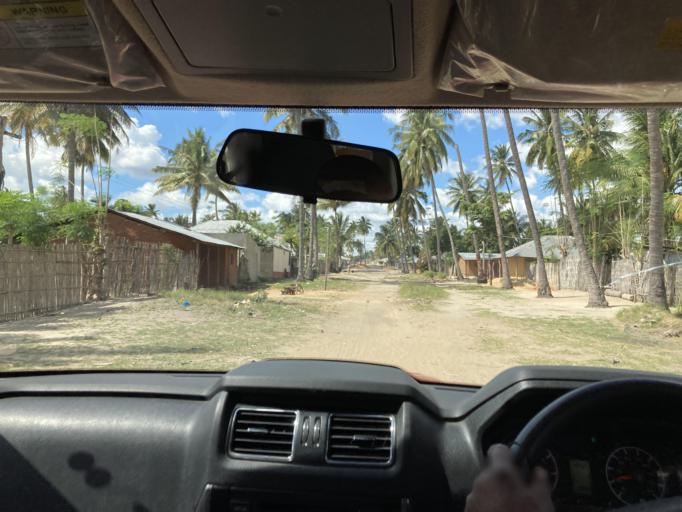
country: MZ
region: Cabo Delgado
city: Montepuez
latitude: -13.1301
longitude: 39.0102
